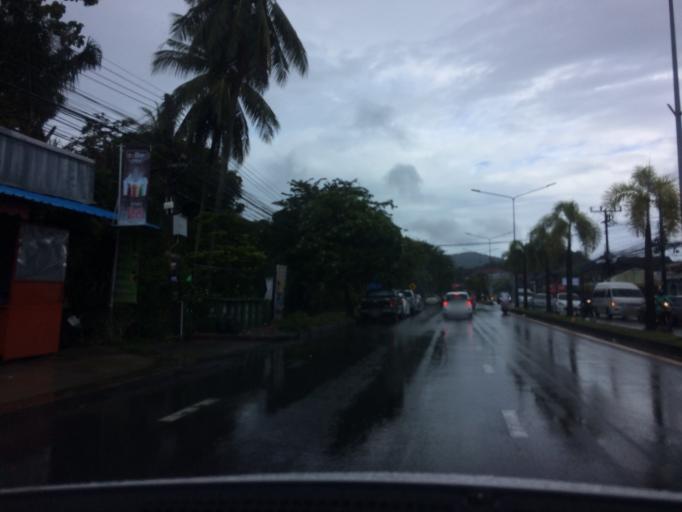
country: TH
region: Phuket
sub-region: Amphoe Kathu
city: Kathu
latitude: 7.9139
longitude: 98.3326
